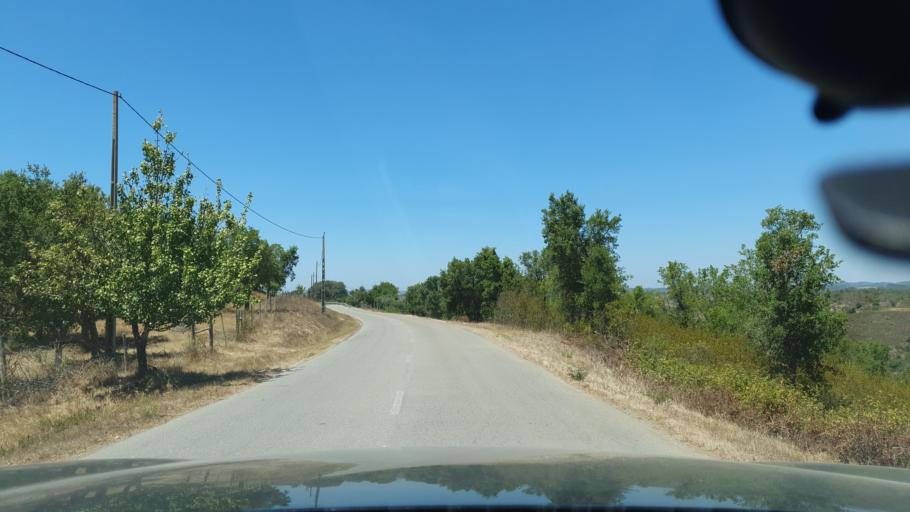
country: PT
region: Beja
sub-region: Odemira
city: Odemira
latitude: 37.5526
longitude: -8.4304
